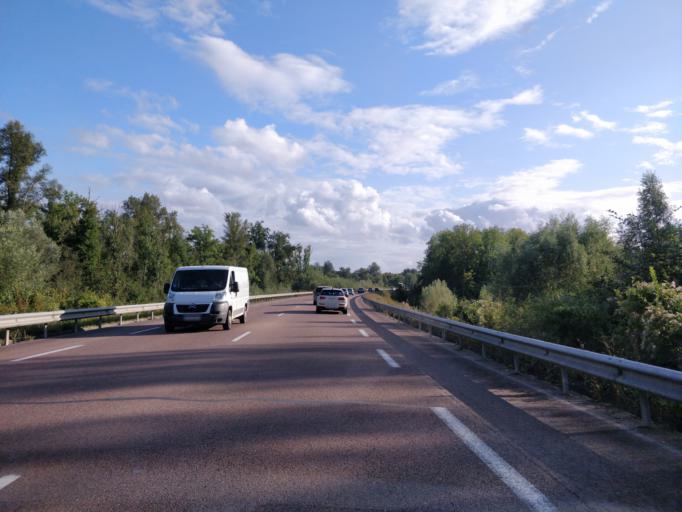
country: FR
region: Champagne-Ardenne
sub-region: Departement de l'Aube
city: Breviandes
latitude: 48.2567
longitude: 4.1160
